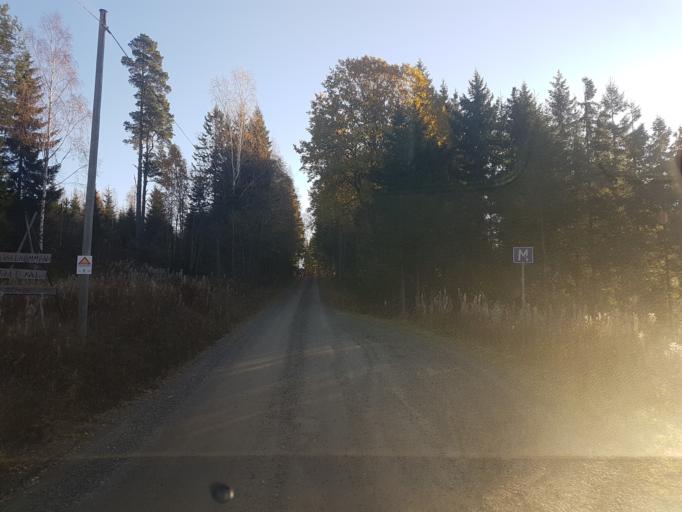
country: SE
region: Vaesternorrland
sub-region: OErnskoeldsviks Kommun
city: Bjasta
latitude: 63.0719
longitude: 18.4317
